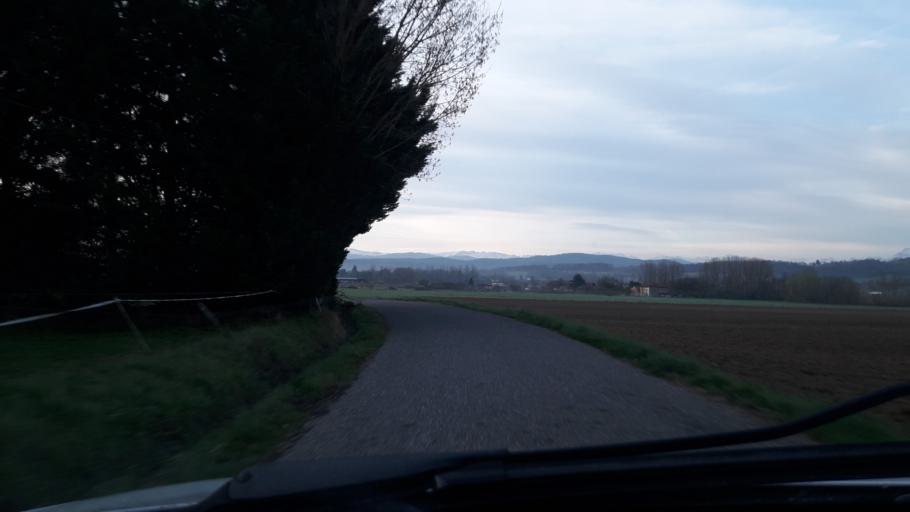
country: FR
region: Midi-Pyrenees
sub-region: Departement de la Haute-Garonne
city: Montesquieu-Volvestre
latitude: 43.1813
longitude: 1.2646
